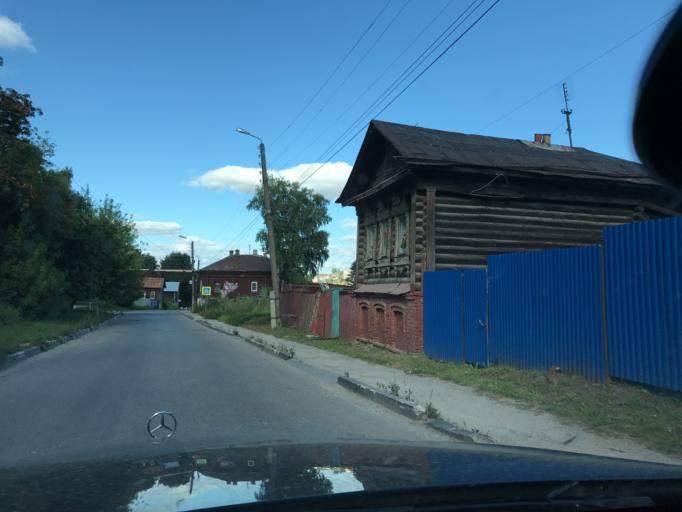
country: RU
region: Nizjnij Novgorod
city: Pavlovo
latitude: 55.9607
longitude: 43.0626
